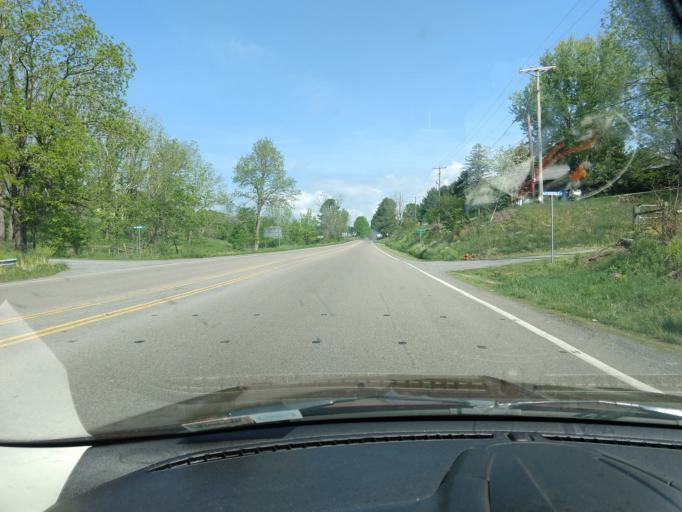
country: US
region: Virginia
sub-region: Russell County
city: Honaker
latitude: 36.9602
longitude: -81.9321
